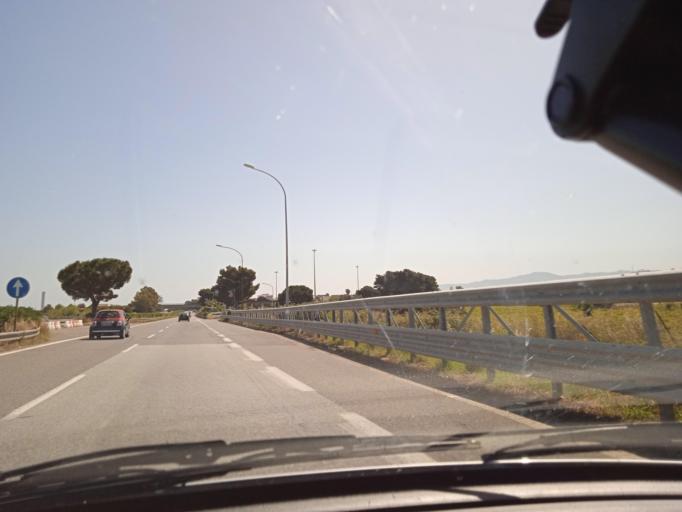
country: IT
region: Sicily
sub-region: Messina
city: Meri
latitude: 38.1808
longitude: 15.2500
